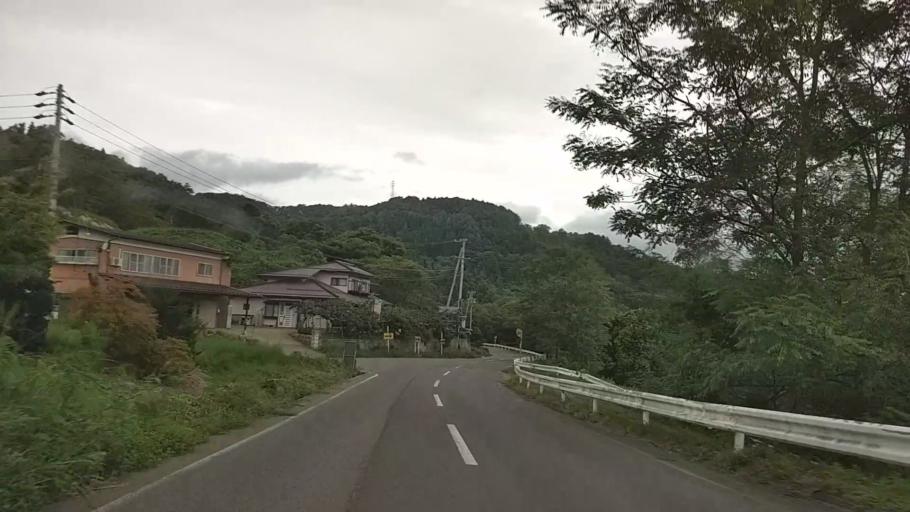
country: JP
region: Nagano
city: Nakano
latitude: 36.7854
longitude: 138.3333
